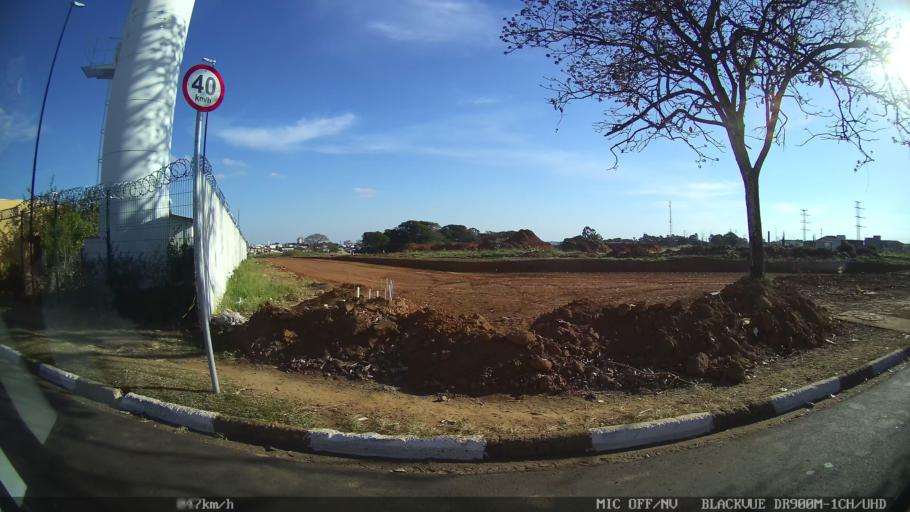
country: BR
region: Sao Paulo
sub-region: Franca
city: Franca
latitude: -20.5148
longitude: -47.3738
